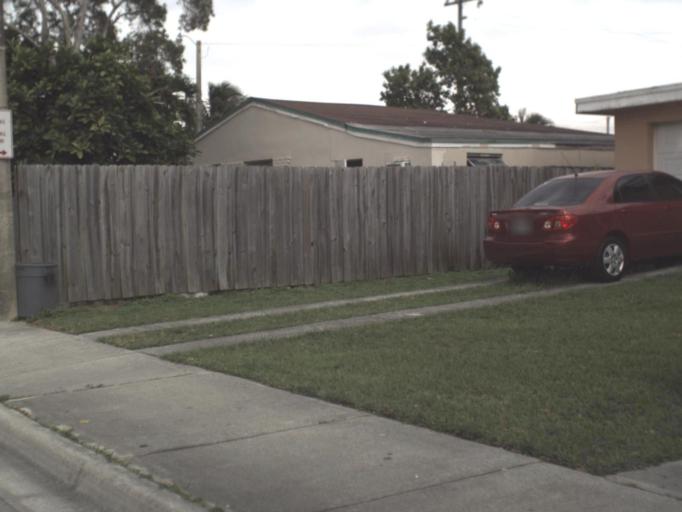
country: US
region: Florida
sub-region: Miami-Dade County
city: Brownsville
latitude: 25.7897
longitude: -80.2559
